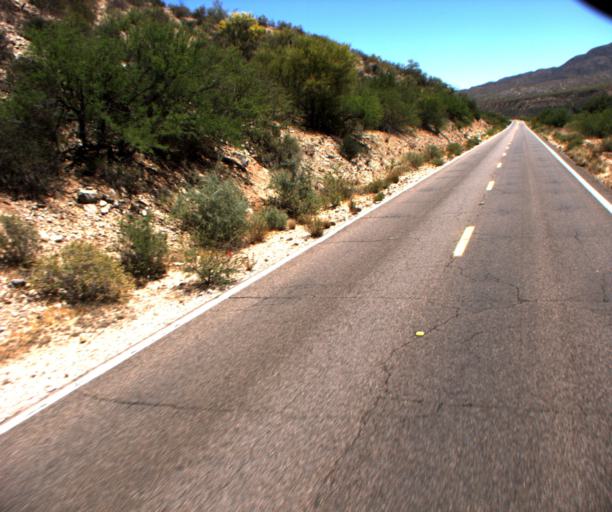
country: US
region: Arizona
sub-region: Pinal County
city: Kearny
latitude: 33.1182
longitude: -110.7719
